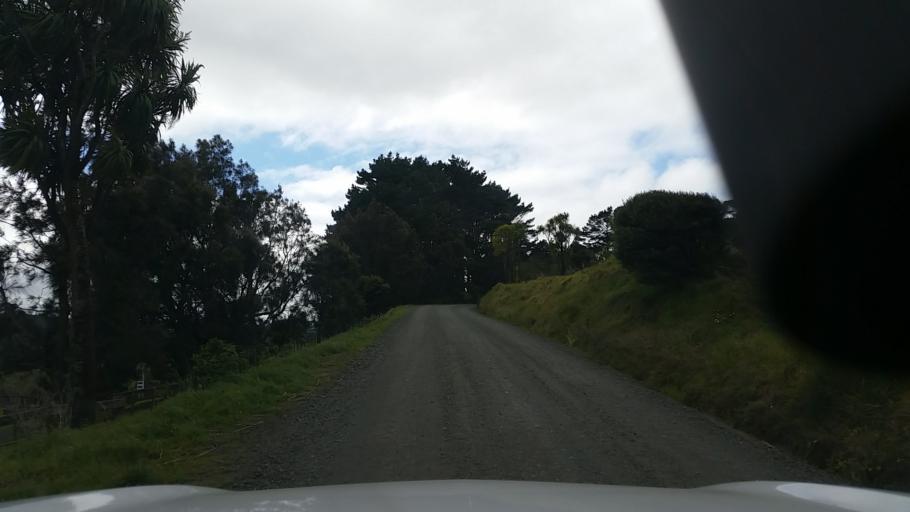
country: NZ
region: Auckland
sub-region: Auckland
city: Muriwai Beach
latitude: -36.8493
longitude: 174.4813
